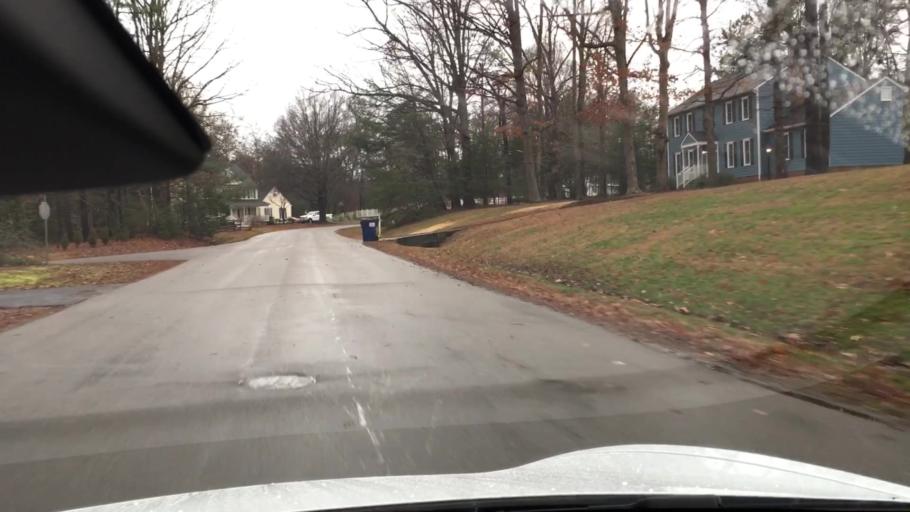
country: US
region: Virginia
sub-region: Chesterfield County
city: Bon Air
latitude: 37.5343
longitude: -77.5967
